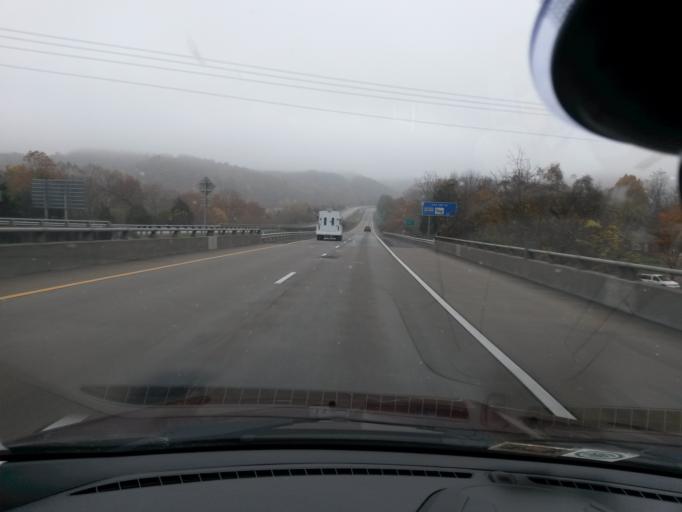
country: US
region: Virginia
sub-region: City of Covington
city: Fairlawn
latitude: 37.7719
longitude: -79.9853
